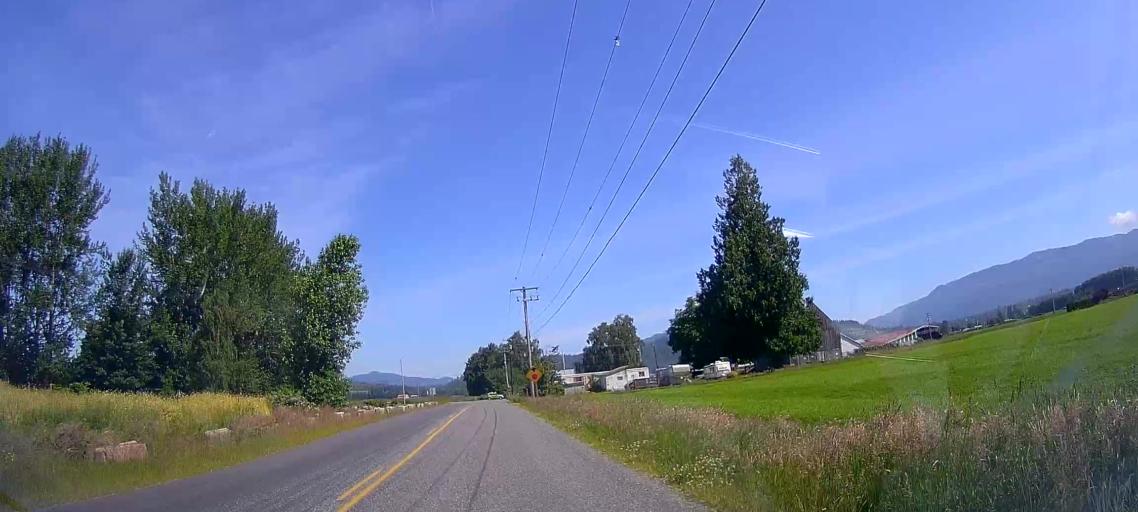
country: US
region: Washington
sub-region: Skagit County
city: Burlington
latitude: 48.5058
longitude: -122.3071
